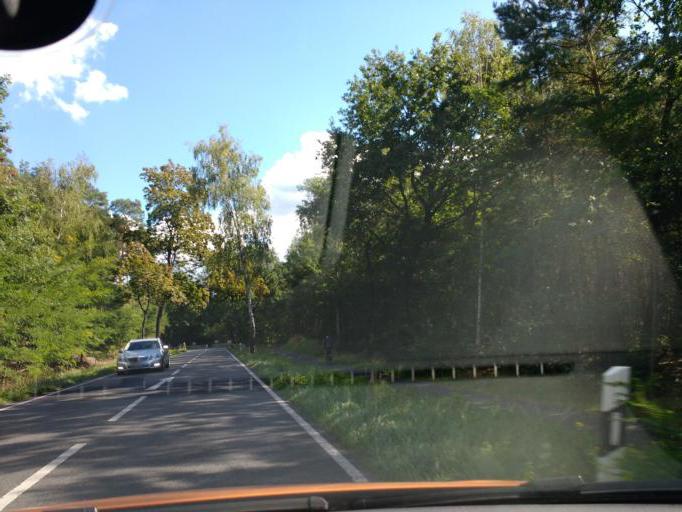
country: DE
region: Brandenburg
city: Bestensee
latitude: 52.2410
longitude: 13.6582
